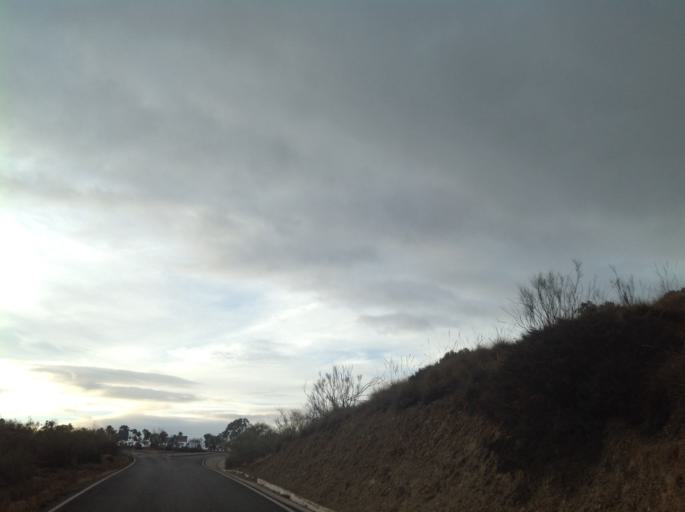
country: ES
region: Andalusia
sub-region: Provincia de Malaga
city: Ardales
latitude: 36.9140
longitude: -4.8060
